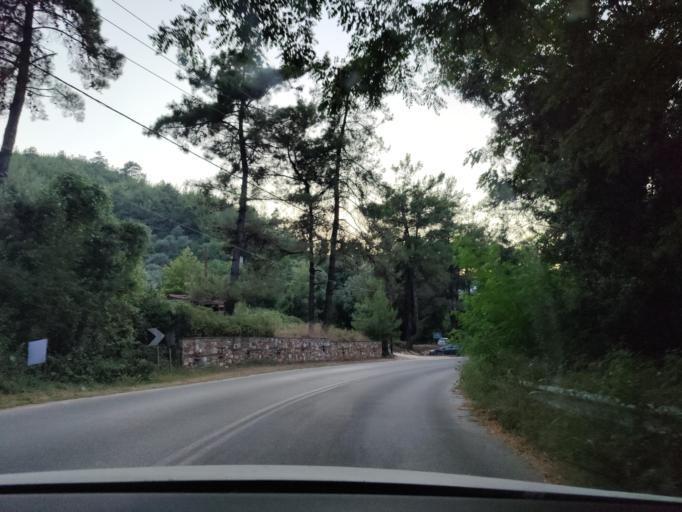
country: GR
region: East Macedonia and Thrace
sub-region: Nomos Kavalas
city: Potamia
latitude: 40.7053
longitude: 24.7622
